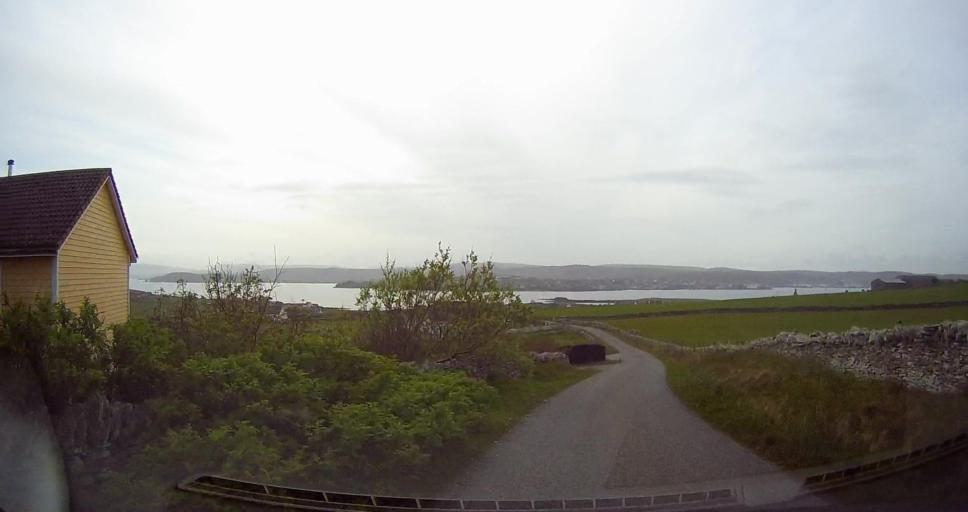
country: GB
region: Scotland
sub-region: Shetland Islands
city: Shetland
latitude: 60.1512
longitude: -1.0993
